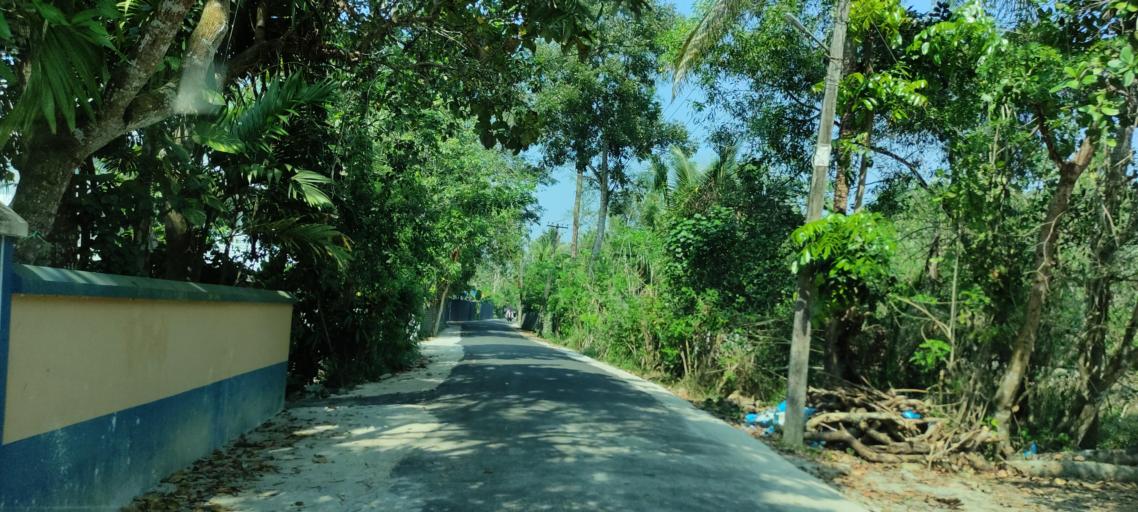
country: IN
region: Kerala
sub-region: Alappuzha
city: Alleppey
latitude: 9.5424
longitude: 76.3206
